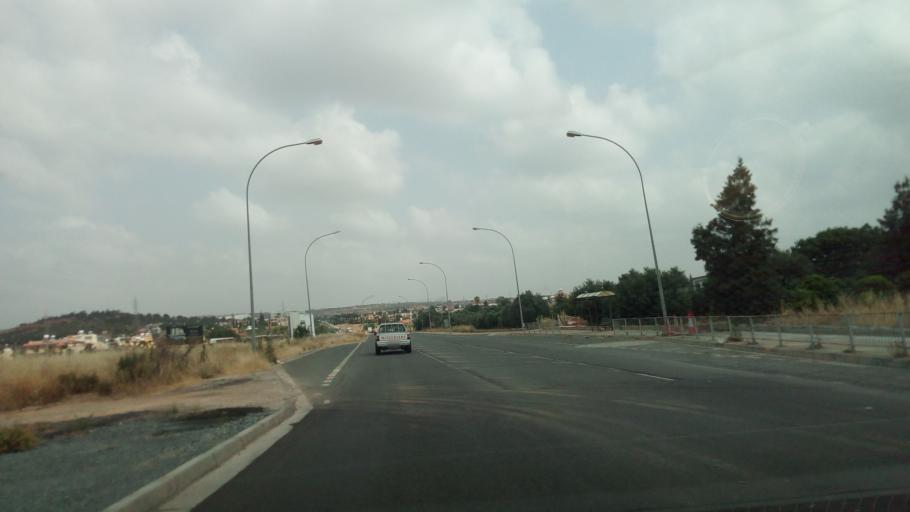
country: CY
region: Limassol
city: Pano Polemidia
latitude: 34.6915
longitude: 32.9887
